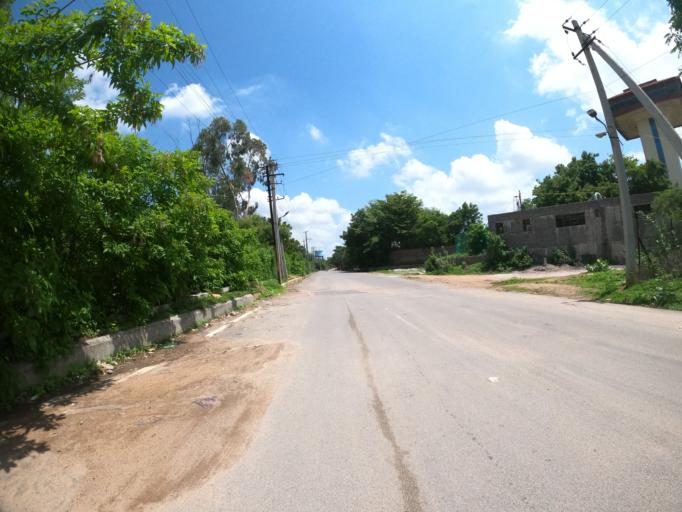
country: IN
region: Telangana
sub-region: Medak
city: Serilingampalle
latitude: 17.3882
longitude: 78.3158
